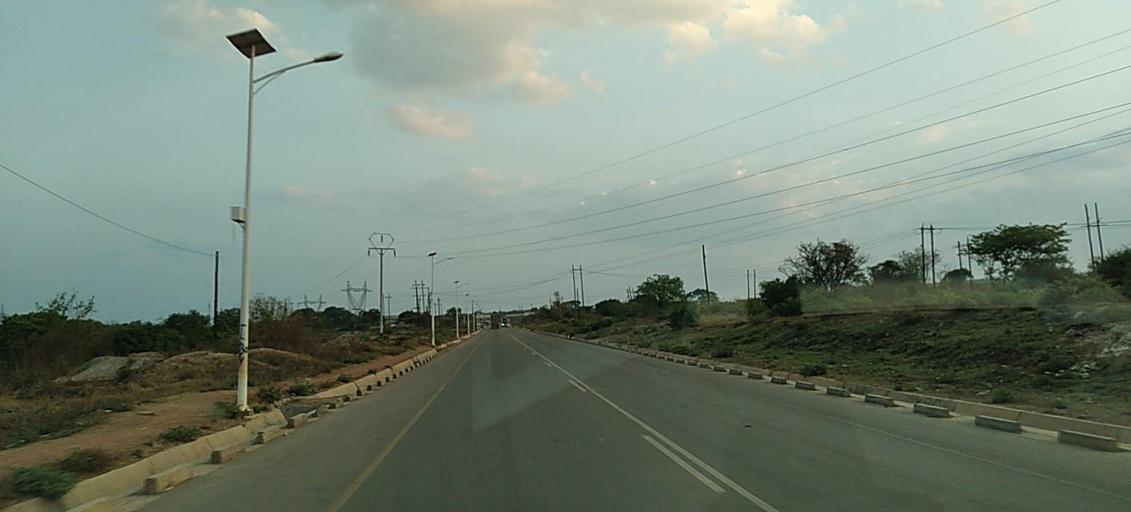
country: ZM
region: Copperbelt
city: Chingola
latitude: -12.5332
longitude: 27.8383
